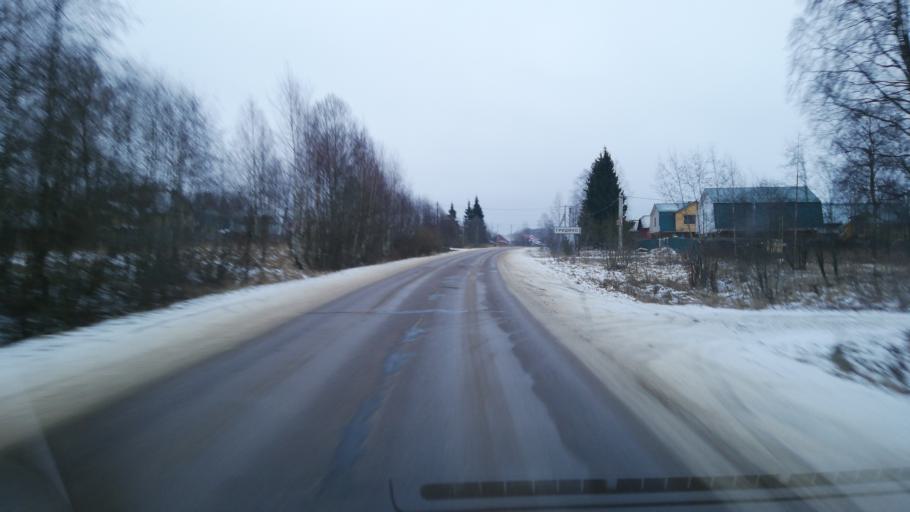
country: RU
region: Kostroma
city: Oktyabr'skiy
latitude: 57.7171
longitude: 41.1375
